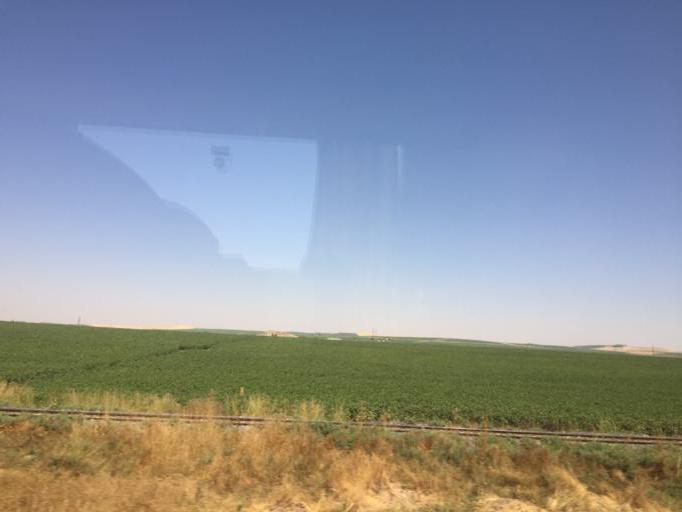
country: TR
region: Diyarbakir
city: Tepe
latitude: 37.8510
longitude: 40.7583
